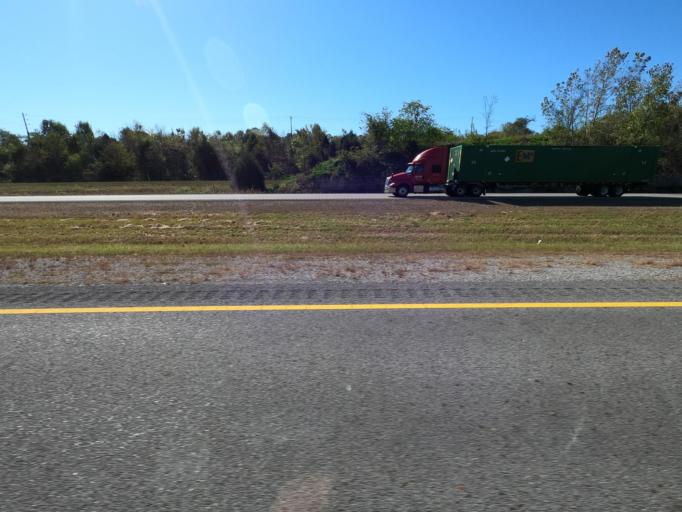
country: US
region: Tennessee
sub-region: Williamson County
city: Thompson's Station
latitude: 35.8218
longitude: -86.8842
